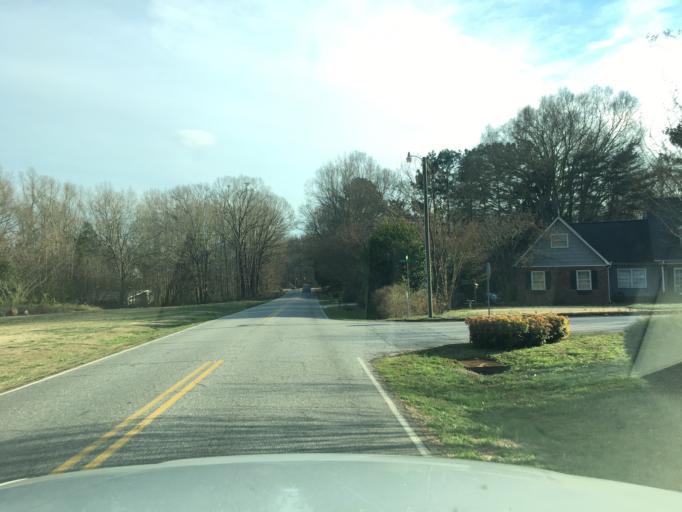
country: US
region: South Carolina
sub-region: Greenville County
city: Wade Hampton
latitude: 34.8621
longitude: -82.2945
